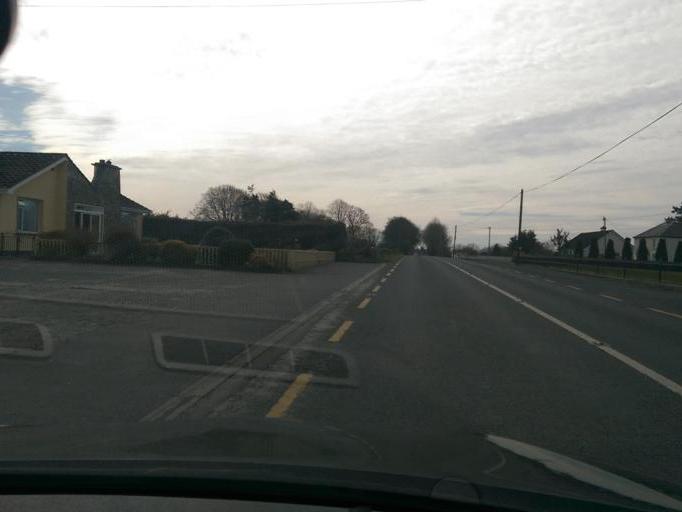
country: IE
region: Connaught
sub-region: County Galway
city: Claregalway
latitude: 53.3940
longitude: -8.8390
